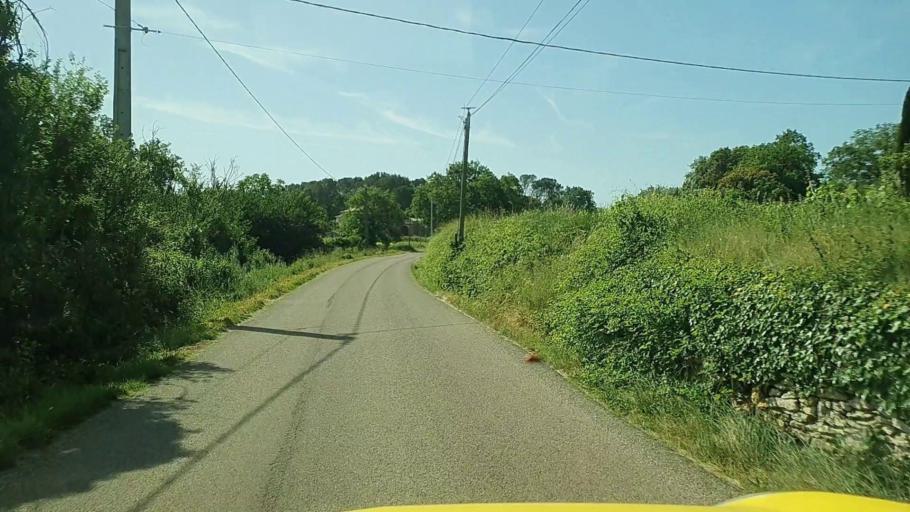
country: FR
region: Languedoc-Roussillon
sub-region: Departement du Gard
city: Sabran
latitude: 44.1369
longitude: 4.4943
